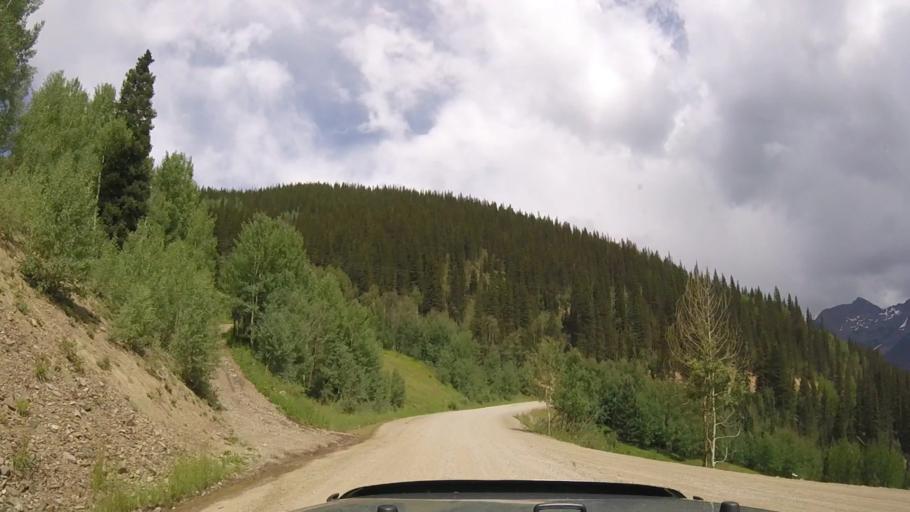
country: US
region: Colorado
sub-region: San Juan County
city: Silverton
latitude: 37.8340
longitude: -107.6735
